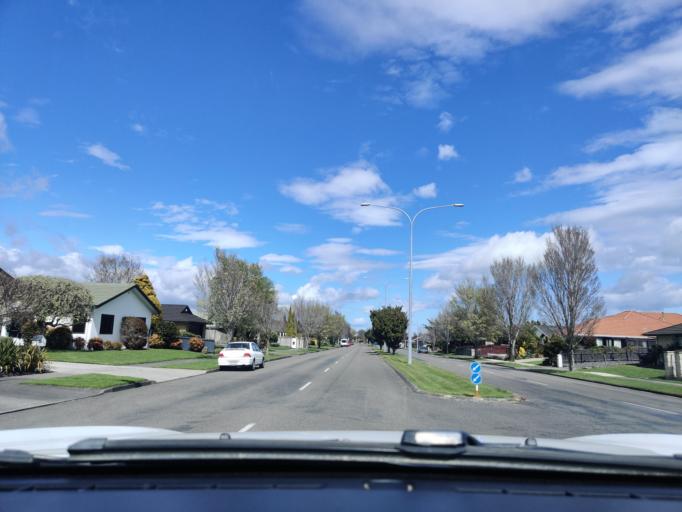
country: NZ
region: Manawatu-Wanganui
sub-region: Palmerston North City
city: Palmerston North
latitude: -40.3248
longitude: 175.6116
